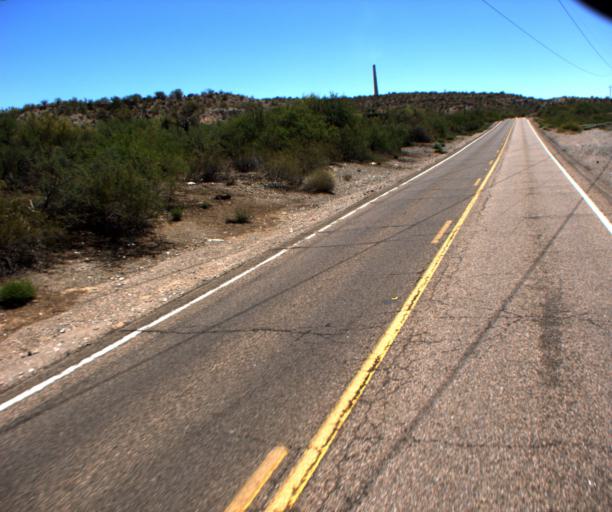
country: US
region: Arizona
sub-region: Pinal County
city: Kearny
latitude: 33.0094
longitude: -110.8055
